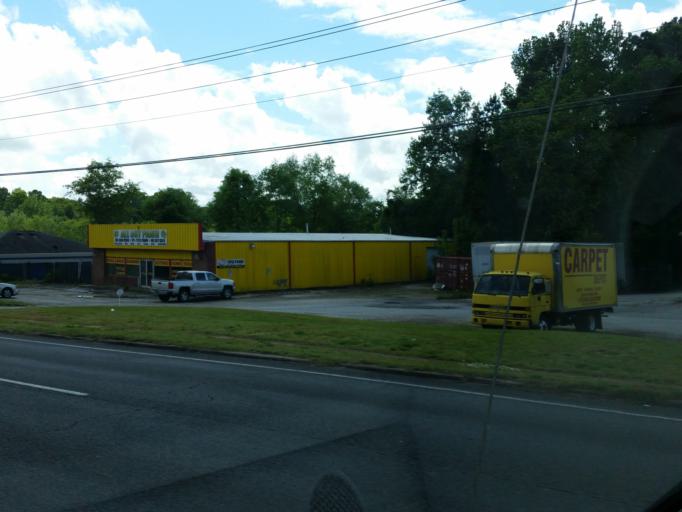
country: US
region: Georgia
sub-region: Clayton County
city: Jonesboro
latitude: 33.5277
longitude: -84.3633
